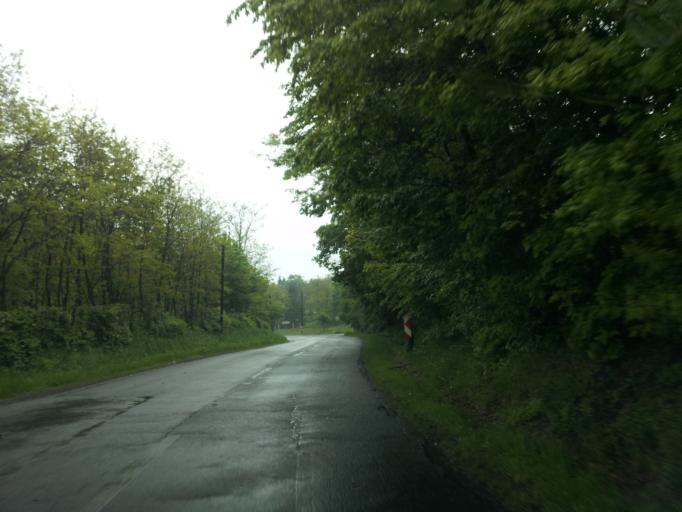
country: HU
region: Baranya
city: Hosszuheteny
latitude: 46.1808
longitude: 18.3191
